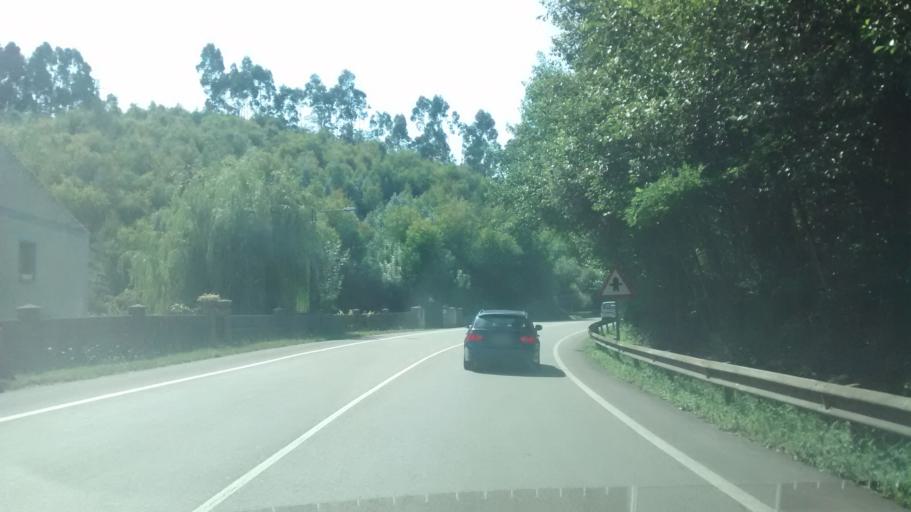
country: ES
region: Cantabria
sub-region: Provincia de Cantabria
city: San Miguel de Meruelo
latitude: 43.4360
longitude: -3.5691
